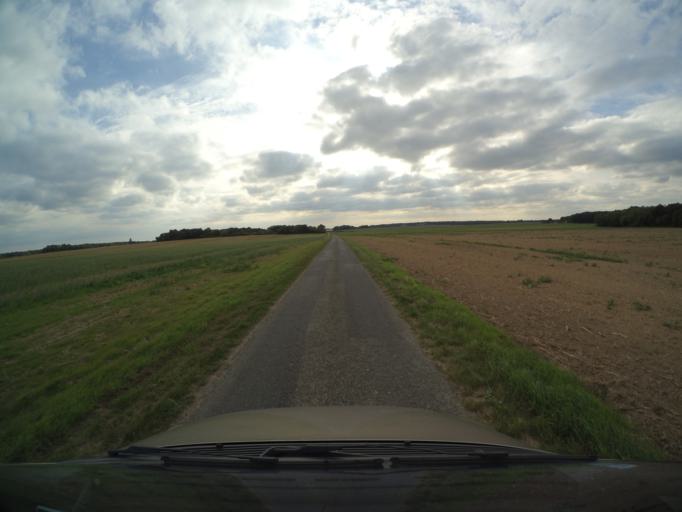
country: FR
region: Centre
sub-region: Departement d'Indre-et-Loire
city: Nazelles-Negron
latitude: 47.4634
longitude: 0.9367
